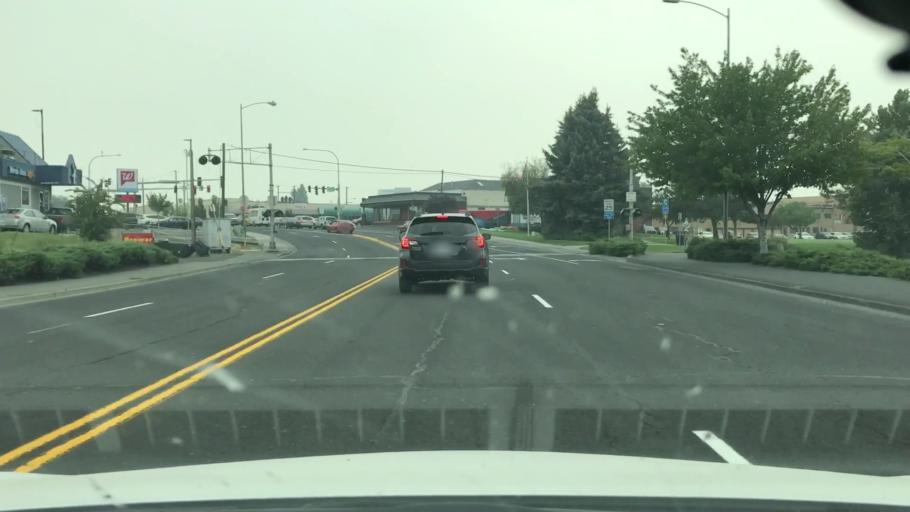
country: US
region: Washington
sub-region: Grant County
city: Moses Lake
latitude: 47.1329
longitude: -119.2784
